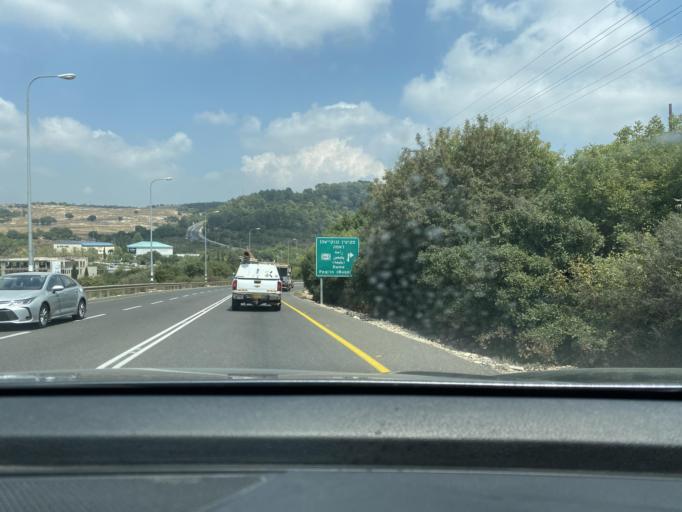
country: IL
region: Northern District
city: Kefar Weradim
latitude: 33.0031
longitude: 35.2906
